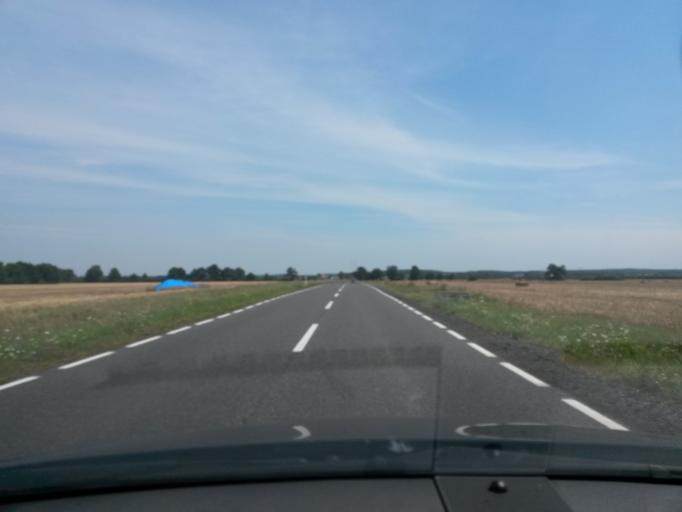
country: PL
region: Lower Silesian Voivodeship
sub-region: Powiat lubinski
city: Scinawa
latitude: 51.4272
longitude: 16.4811
